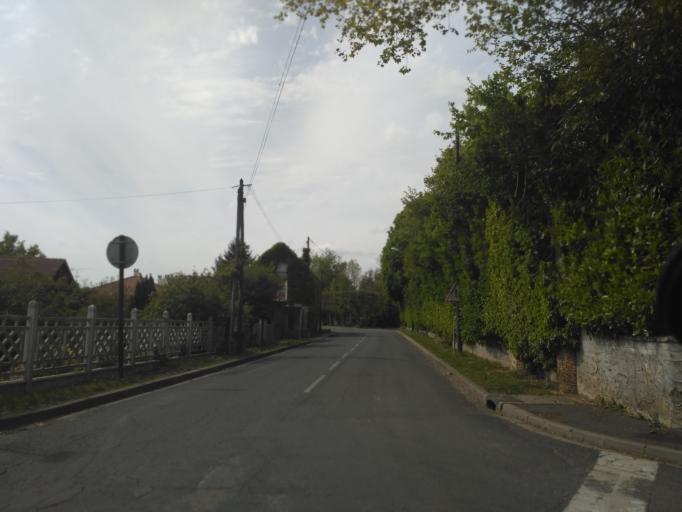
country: FR
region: Ile-de-France
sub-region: Departement de Seine-et-Marne
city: Chaumes-en-Brie
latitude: 48.6653
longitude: 2.8356
